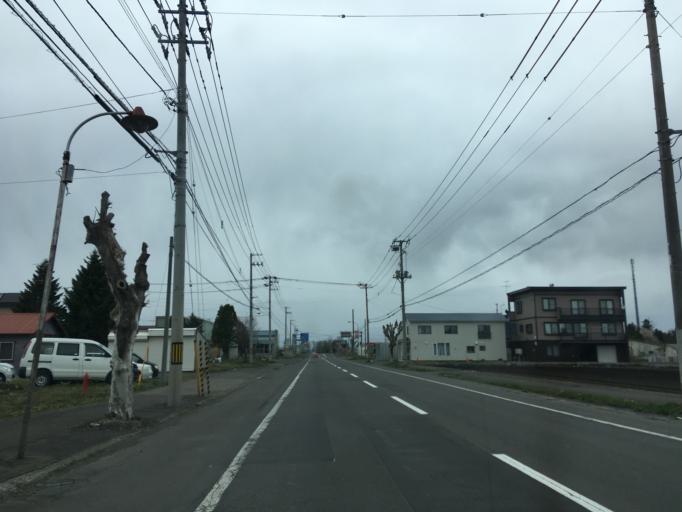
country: JP
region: Hokkaido
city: Chitose
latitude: 42.9475
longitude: 141.8031
